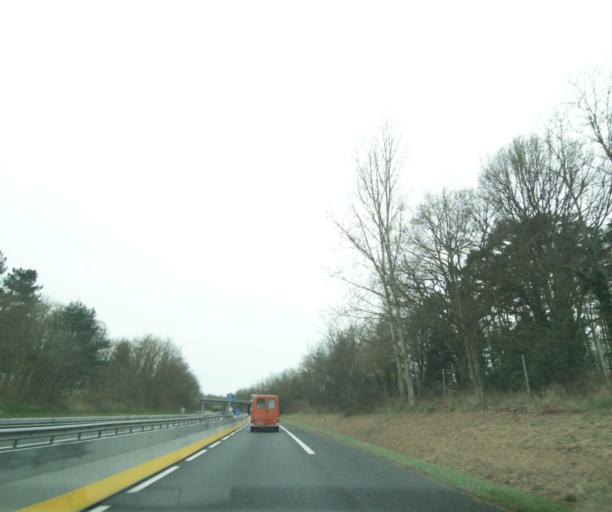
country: FR
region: Centre
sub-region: Departement du Cher
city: Vierzon
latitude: 47.2365
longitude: 2.0371
